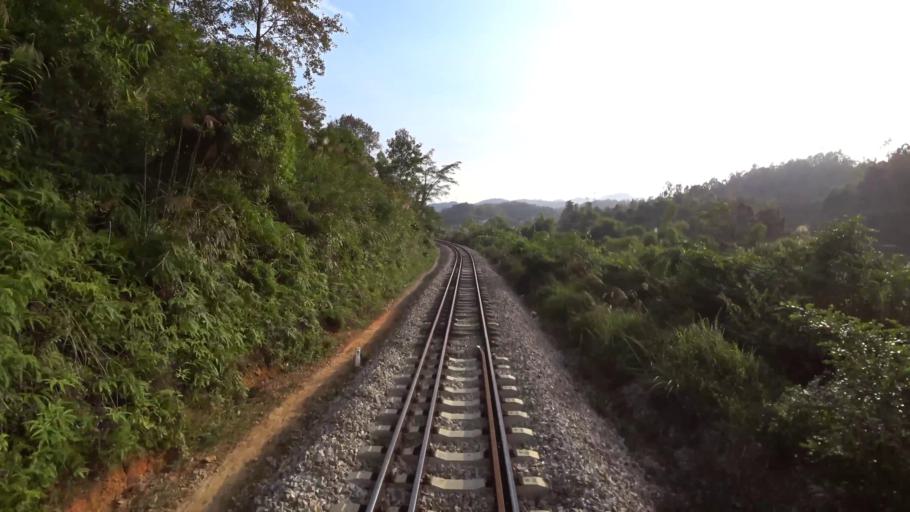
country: VN
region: Lang Son
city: Thi Tran Cao Loc
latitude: 21.9237
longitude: 106.7064
